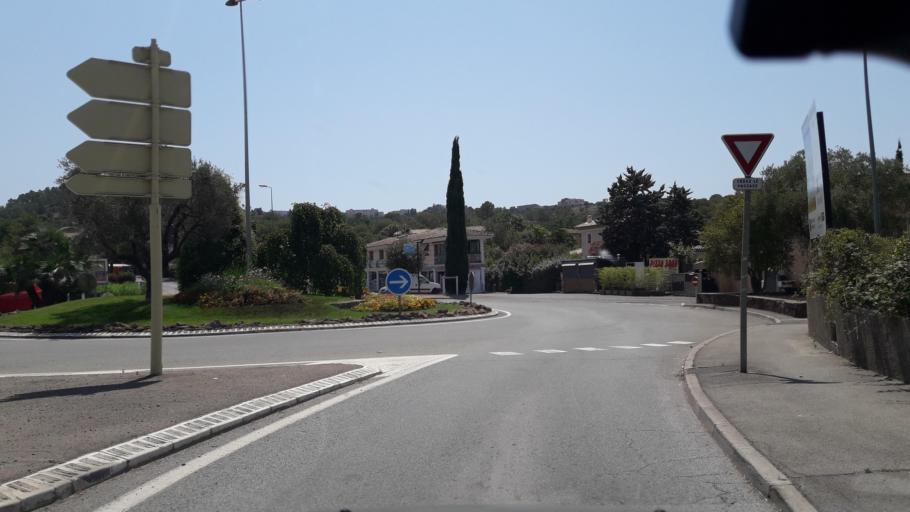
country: FR
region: Provence-Alpes-Cote d'Azur
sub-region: Departement du Var
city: Saint-Raphael
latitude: 43.4384
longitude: 6.7834
